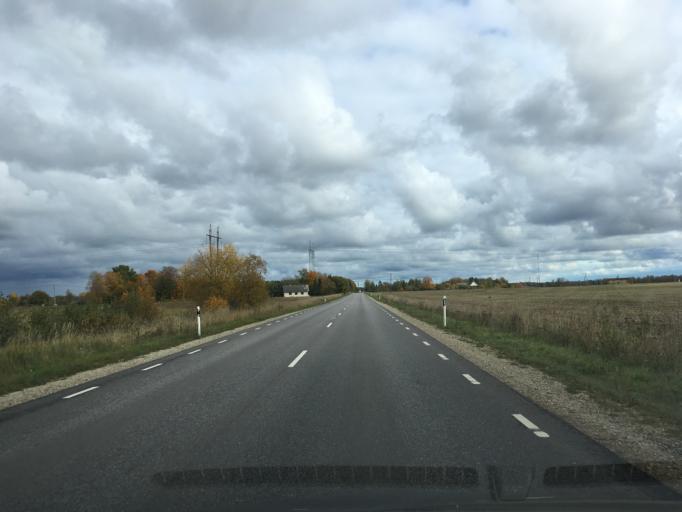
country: EE
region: Harju
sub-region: Anija vald
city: Kehra
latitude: 59.2478
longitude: 25.3077
